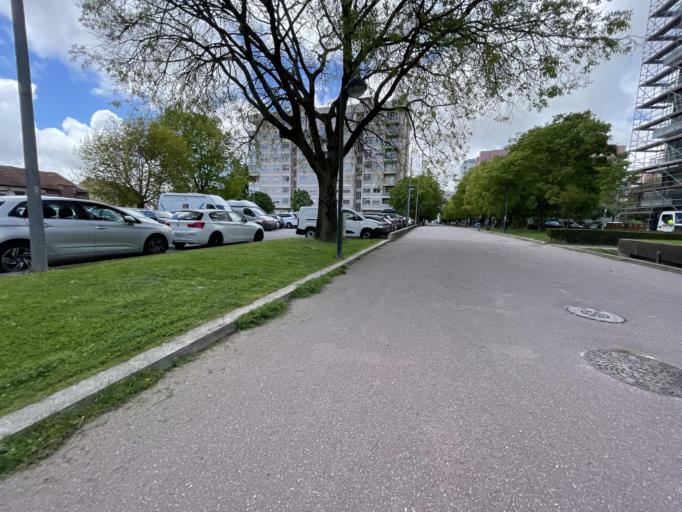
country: PT
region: Porto
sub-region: Porto
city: Porto
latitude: 41.1629
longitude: -8.5958
